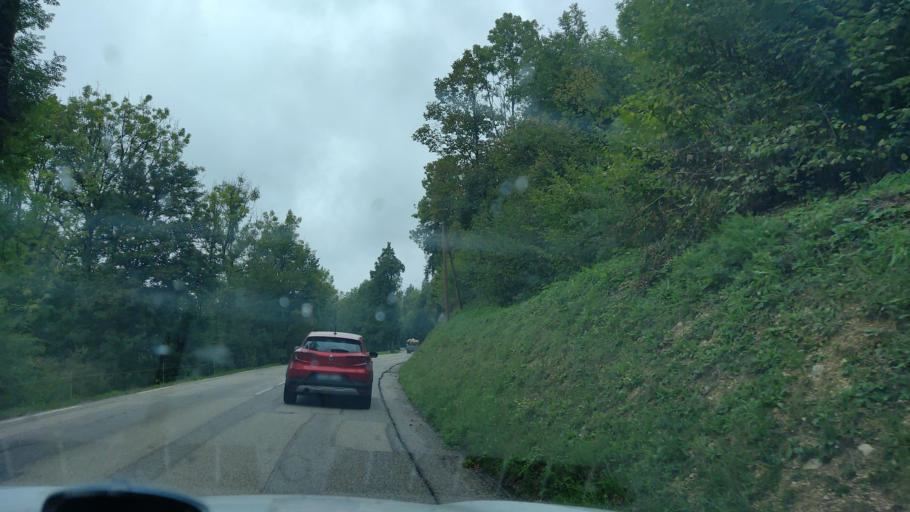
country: FR
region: Rhone-Alpes
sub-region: Departement de l'Isere
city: Barraux
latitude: 45.4413
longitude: 5.8796
